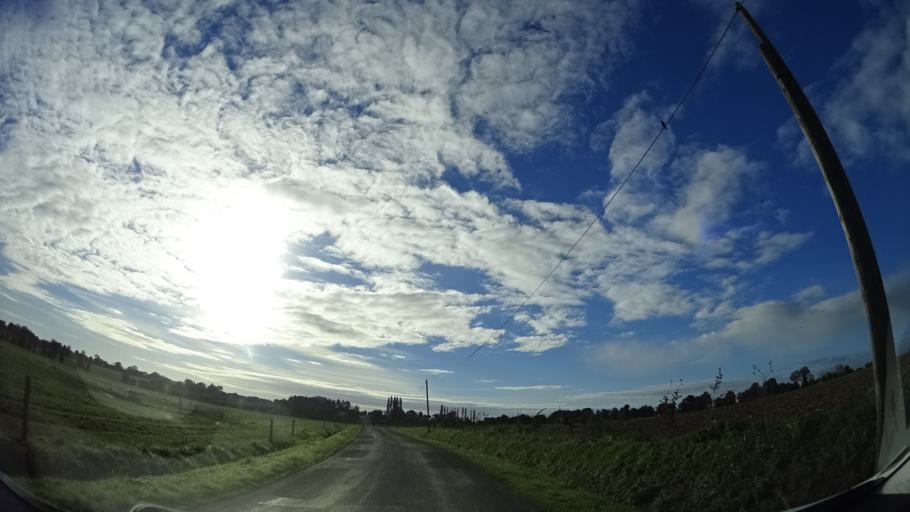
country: FR
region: Brittany
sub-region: Departement d'Ille-et-Vilaine
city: Geveze
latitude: 48.1968
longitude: -1.8201
